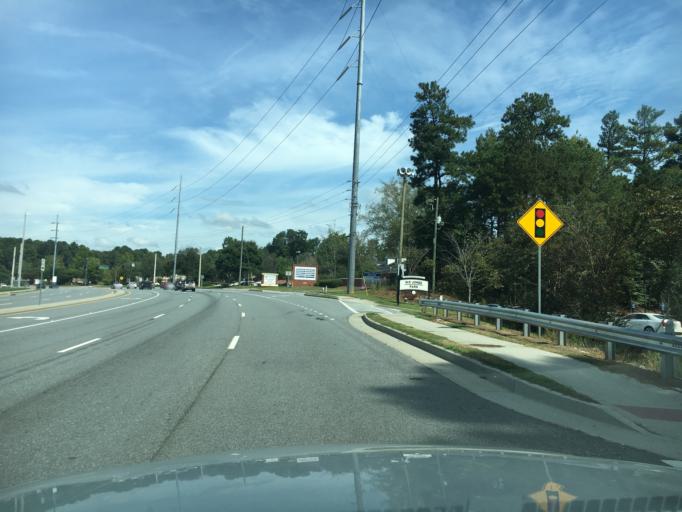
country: US
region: Georgia
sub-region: Gwinnett County
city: Duluth
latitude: 33.9990
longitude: -84.1614
